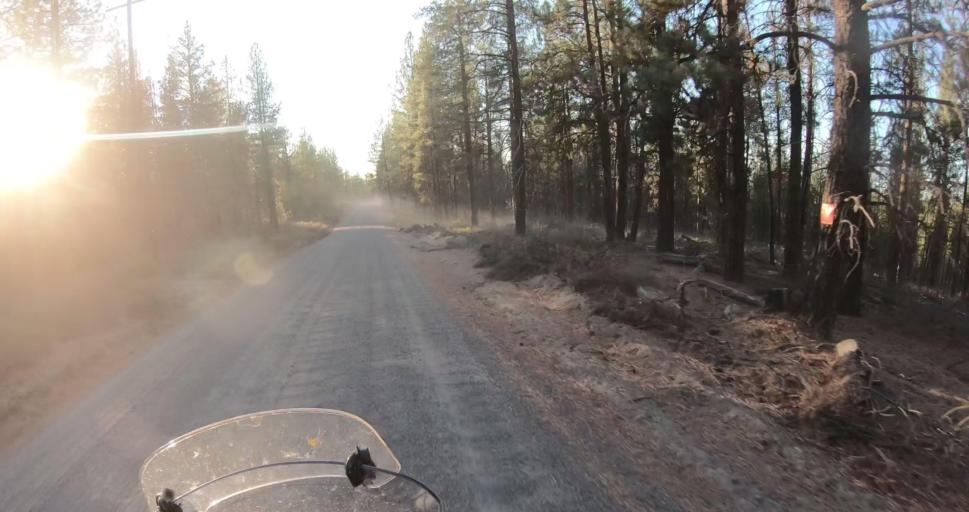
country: US
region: Oregon
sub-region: Deschutes County
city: La Pine
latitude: 43.7198
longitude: -121.3952
